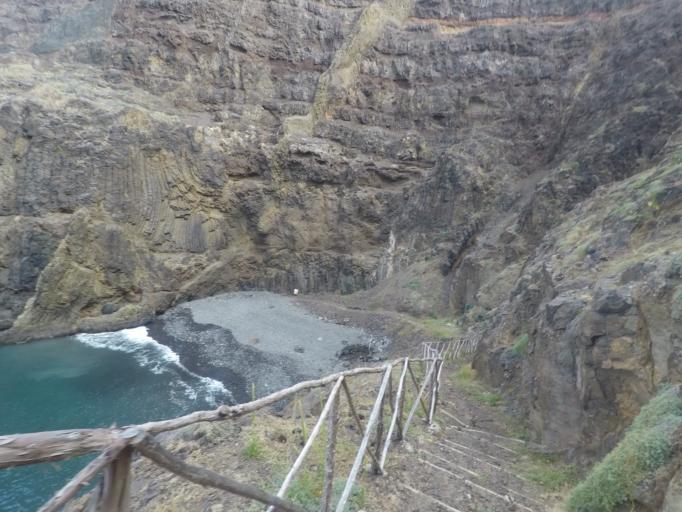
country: PT
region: Madeira
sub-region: Porto Santo
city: Vila de Porto Santo
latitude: 33.0325
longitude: -16.3871
